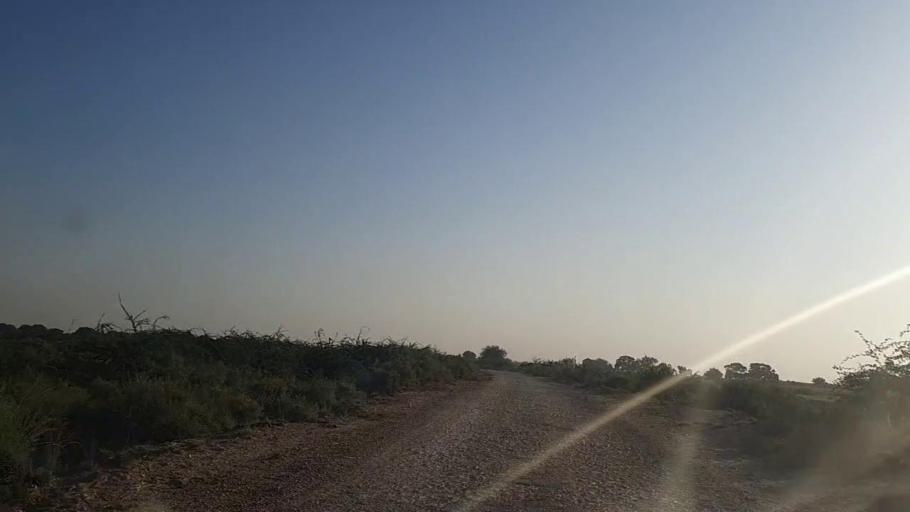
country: PK
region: Sindh
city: Jati
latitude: 24.4348
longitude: 68.1918
